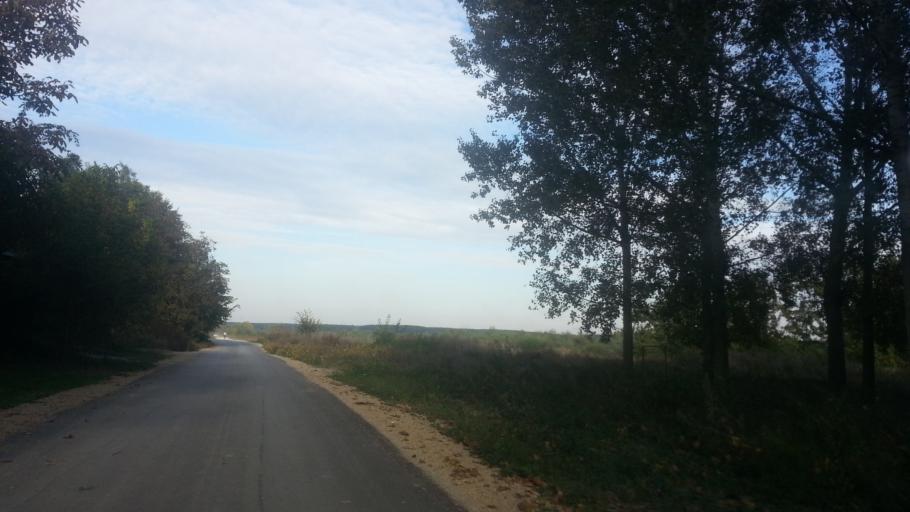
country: RS
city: Belegis
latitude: 45.0194
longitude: 20.3468
